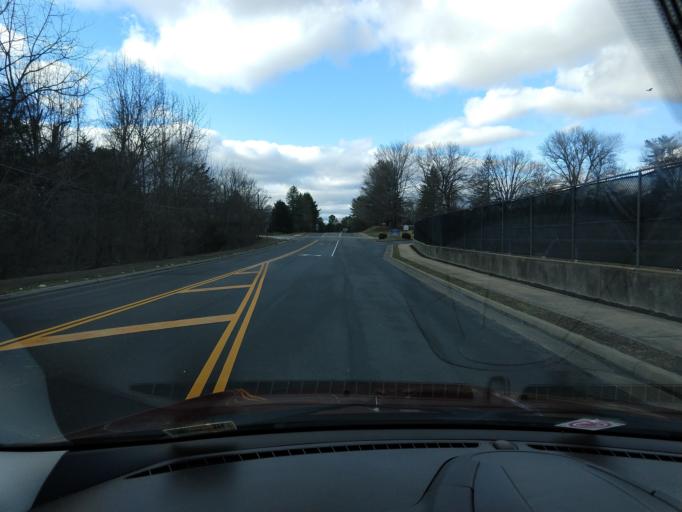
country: US
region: Virginia
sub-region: City of Lexington
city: Lexington
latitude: 37.7922
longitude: -79.4509
